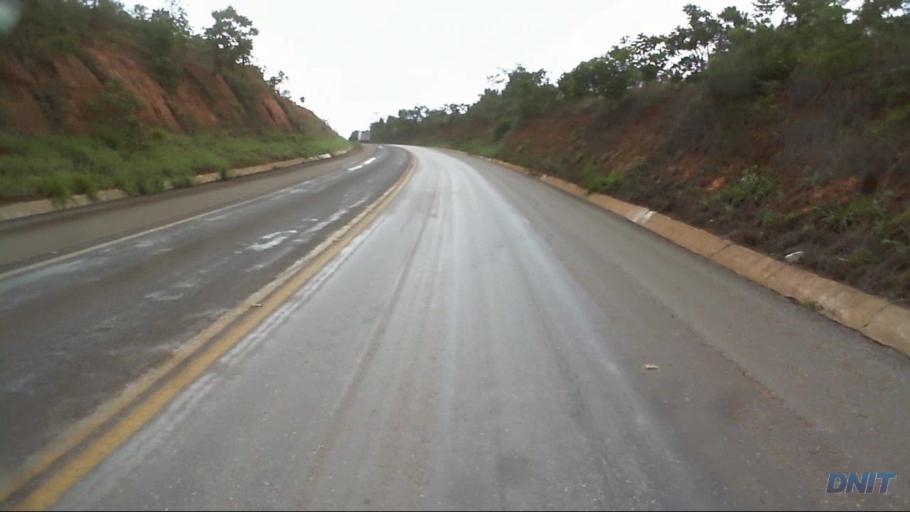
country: BR
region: Goias
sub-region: Barro Alto
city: Barro Alto
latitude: -14.9362
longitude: -48.9466
